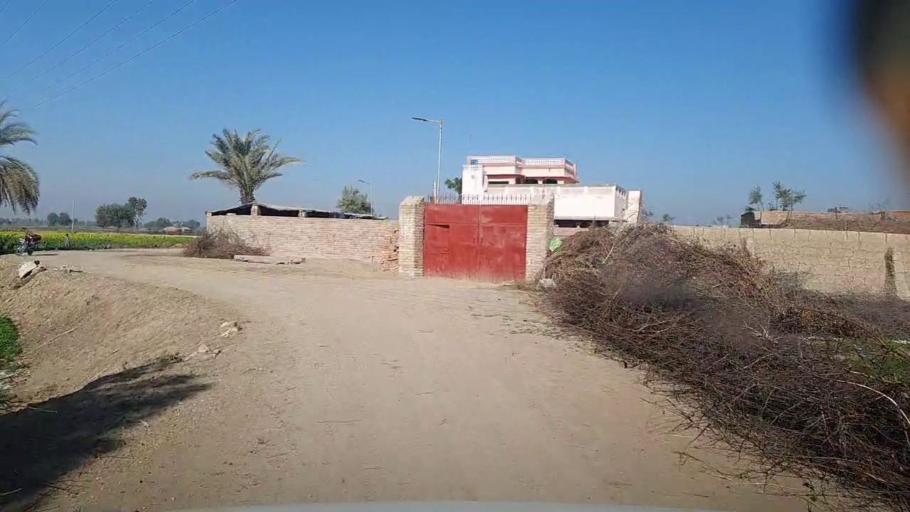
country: PK
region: Sindh
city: Khairpur
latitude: 28.0601
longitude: 69.7396
